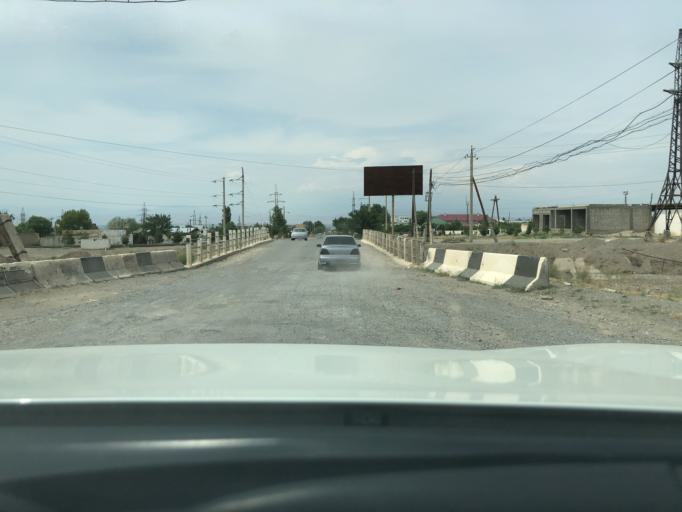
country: TJ
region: Viloyati Sughd
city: Konibodom
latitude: 40.2739
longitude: 70.4465
